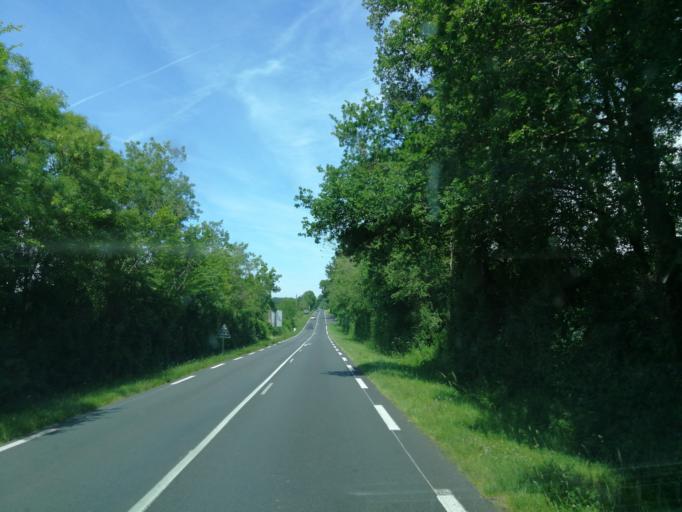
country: FR
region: Pays de la Loire
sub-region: Departement de la Vendee
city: Pissotte
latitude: 46.5172
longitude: -0.8080
